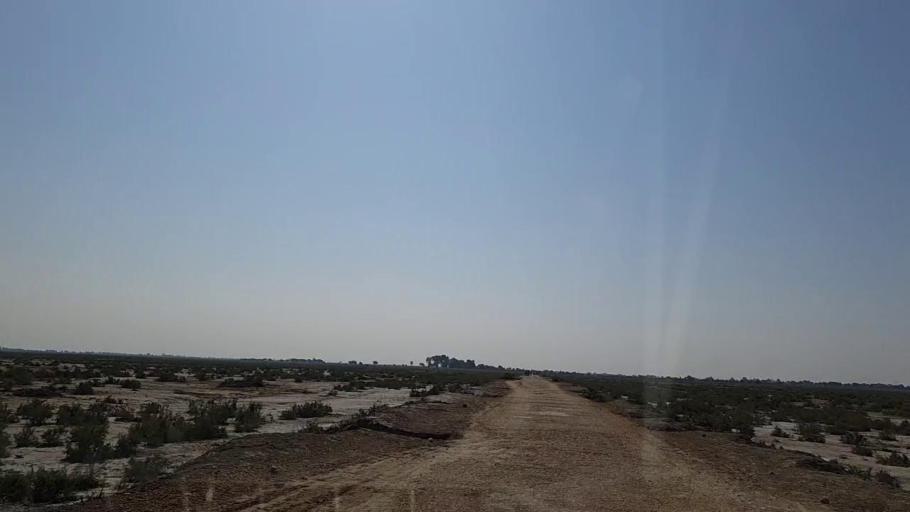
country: PK
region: Sindh
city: Chuhar Jamali
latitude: 24.5069
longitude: 68.0980
